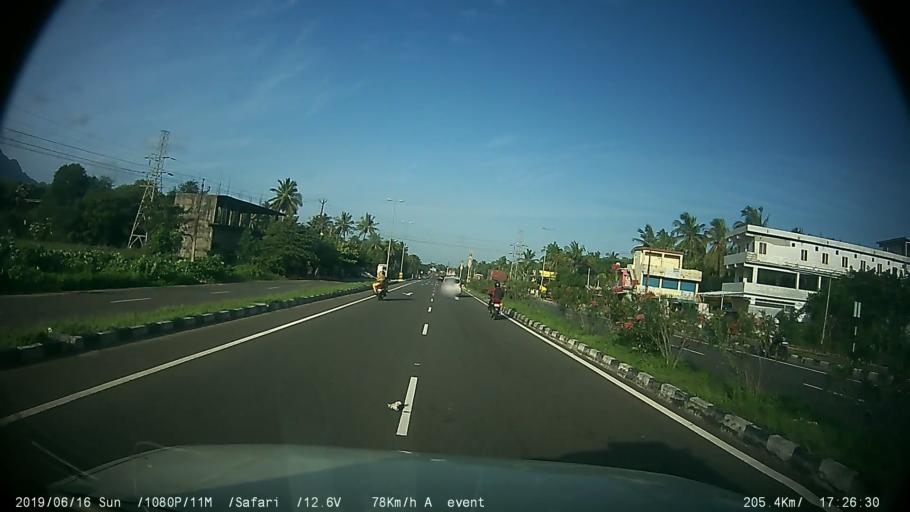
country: IN
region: Kerala
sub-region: Palakkad district
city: Palakkad
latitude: 10.7991
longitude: 76.7527
